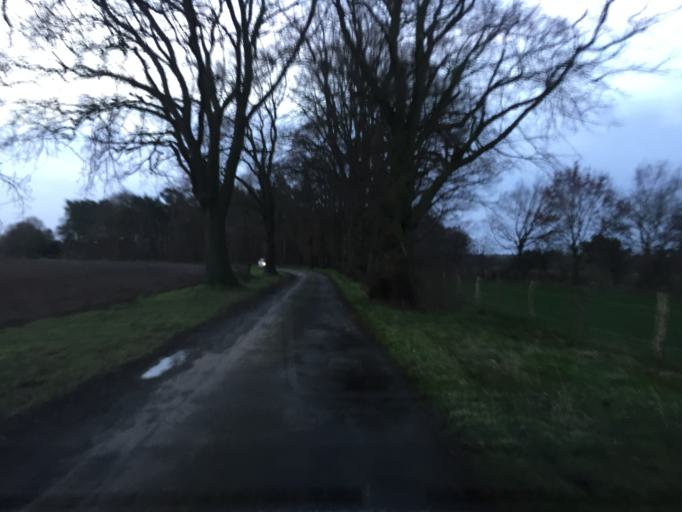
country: DE
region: Lower Saxony
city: Kirchdorf
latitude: 52.6127
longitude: 8.8650
